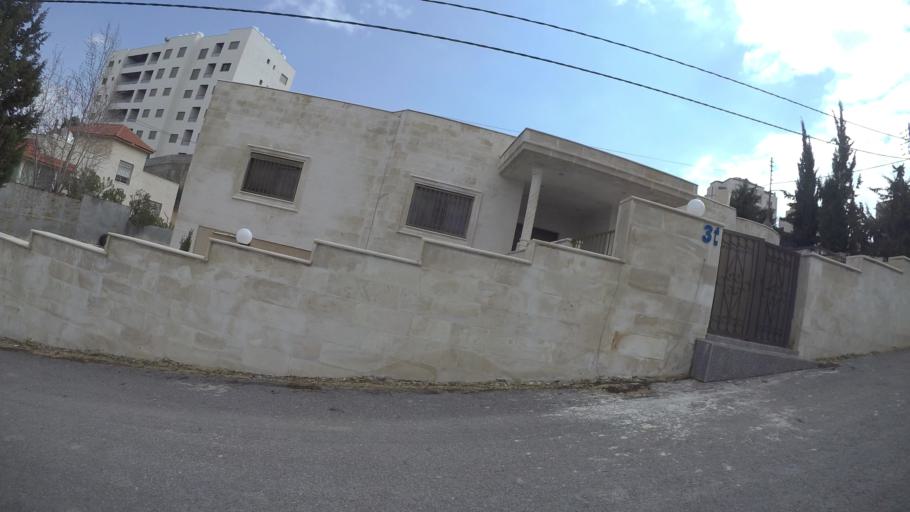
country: JO
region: Amman
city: Al Jubayhah
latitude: 32.0363
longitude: 35.8179
